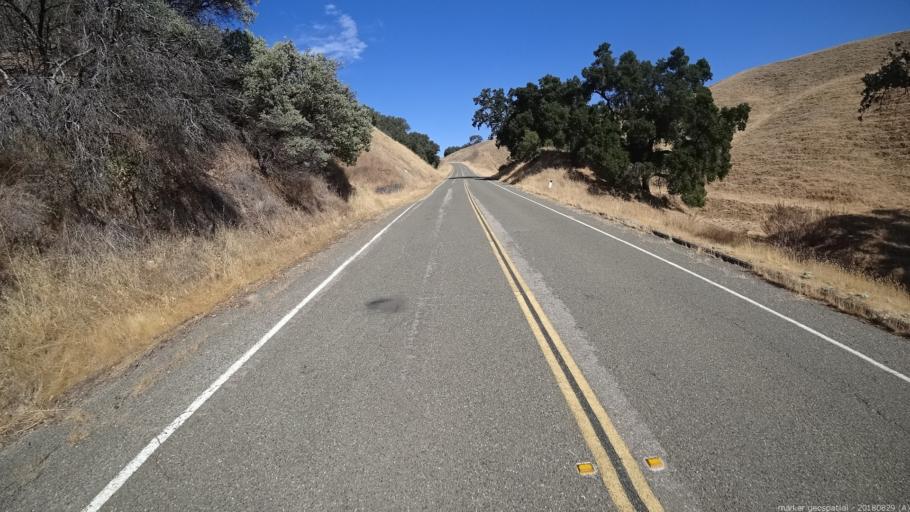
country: US
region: California
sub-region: San Luis Obispo County
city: Lake Nacimiento
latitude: 35.8425
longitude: -121.0453
